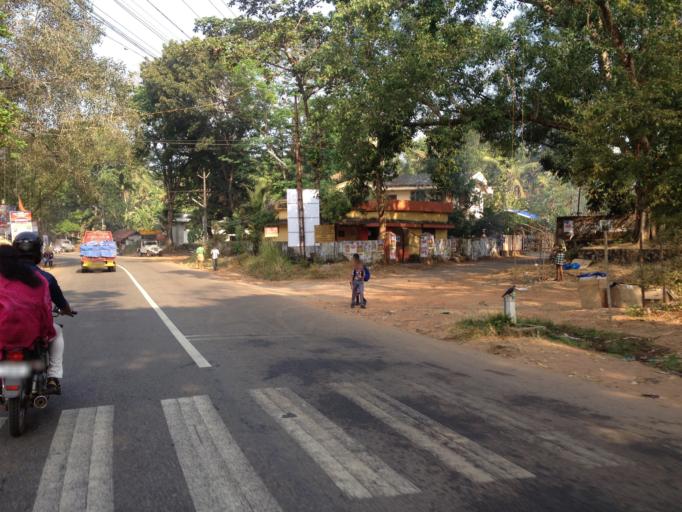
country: IN
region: Kerala
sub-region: Pattanamtitta
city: Adur
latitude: 9.1605
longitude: 76.7155
